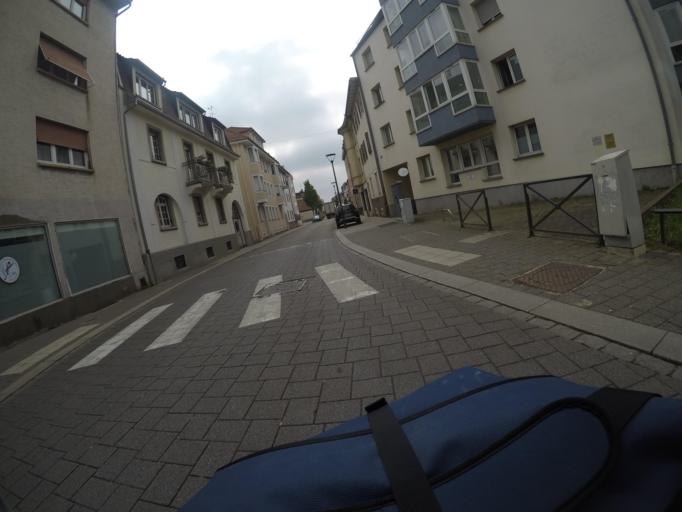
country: FR
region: Alsace
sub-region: Departement du Bas-Rhin
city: Strasbourg
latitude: 48.5934
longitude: 7.7216
